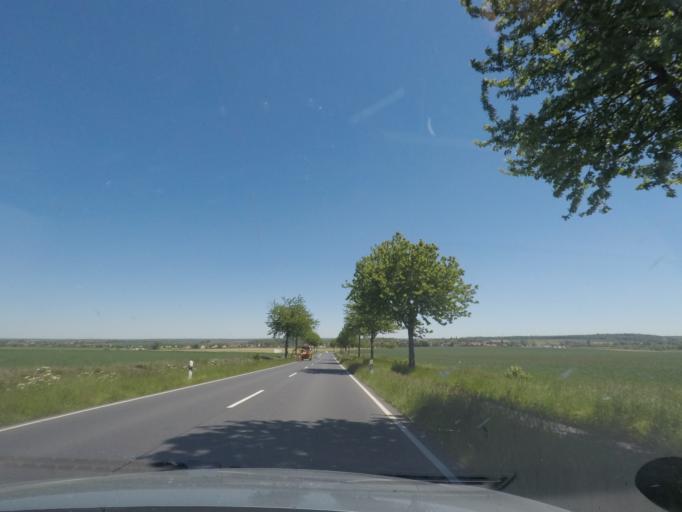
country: DE
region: Lower Saxony
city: Supplingen
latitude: 52.2269
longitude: 10.8846
